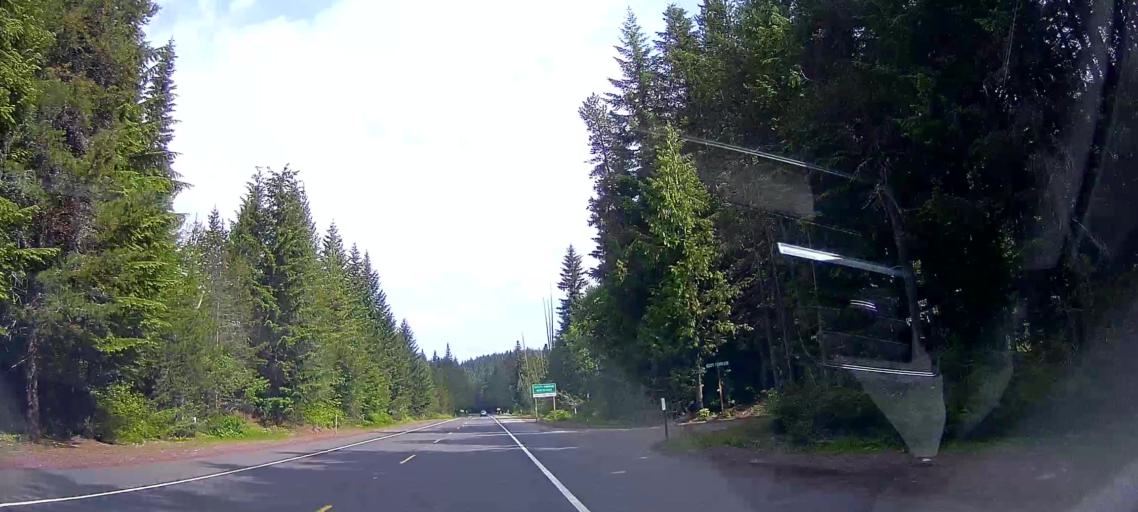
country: US
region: Oregon
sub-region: Clackamas County
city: Mount Hood Village
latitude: 45.2539
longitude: -121.7113
